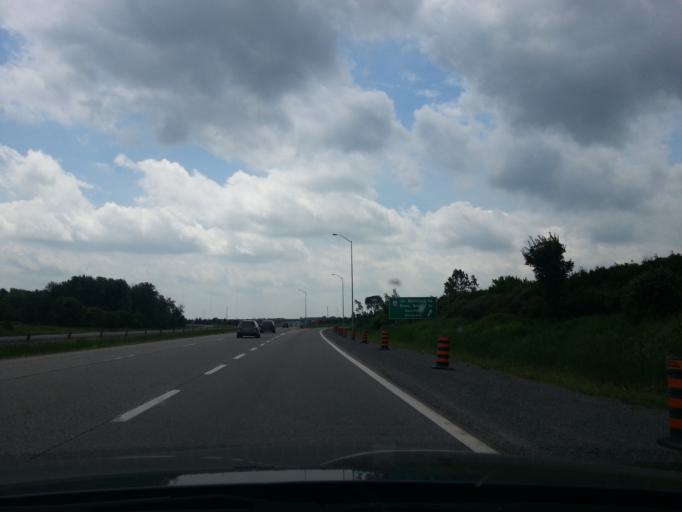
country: CA
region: Ontario
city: Bells Corners
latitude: 45.2144
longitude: -75.7412
